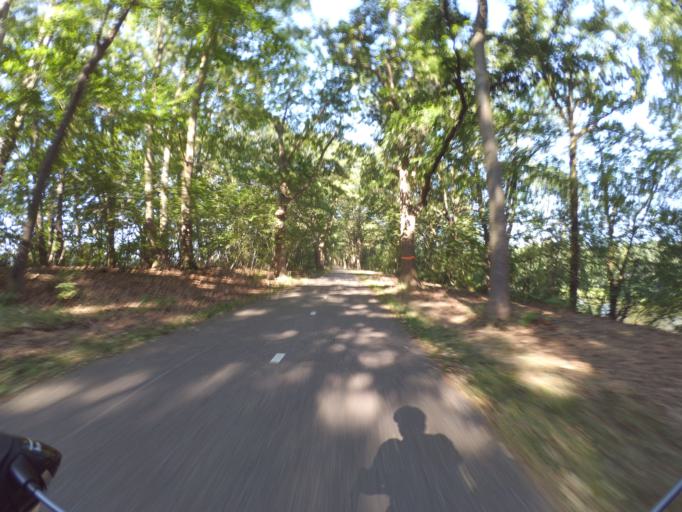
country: NL
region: North Brabant
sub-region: Gemeente Made en Drimmelen
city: Made
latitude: 51.6462
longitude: 4.8186
